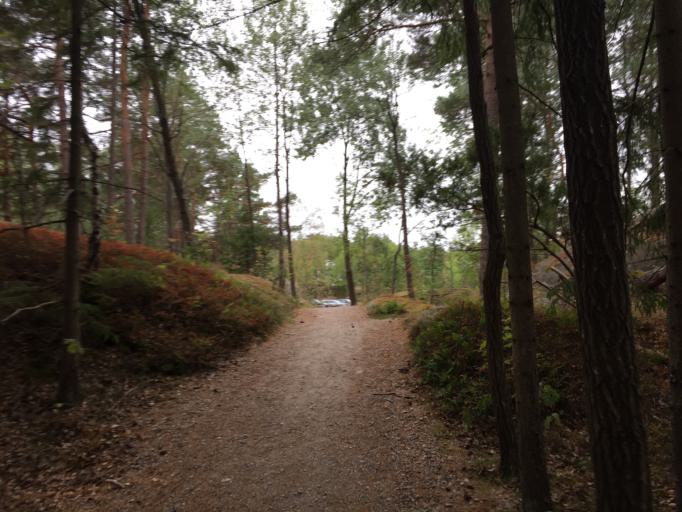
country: NO
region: Ostfold
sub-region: Hvaler
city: Skjaerhalden
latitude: 59.0845
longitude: 11.0001
